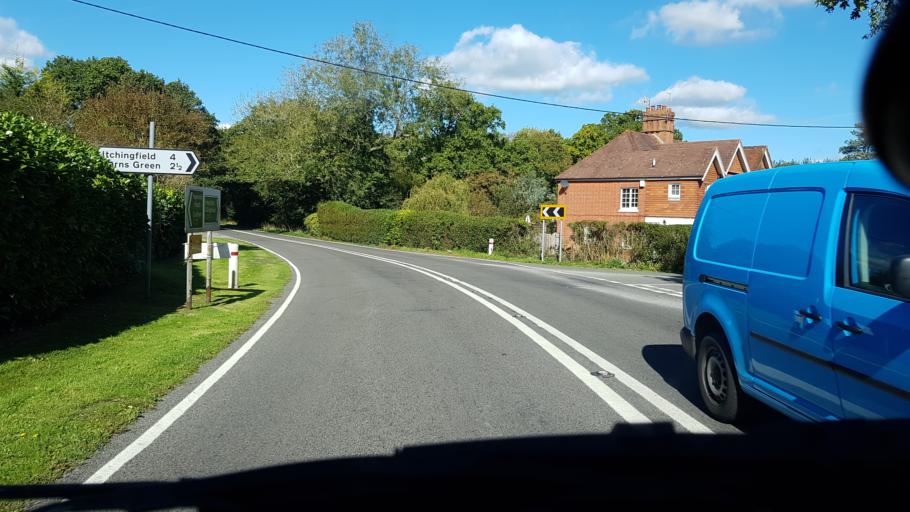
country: GB
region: England
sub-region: West Sussex
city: Billingshurst
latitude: 51.0051
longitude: -0.4274
